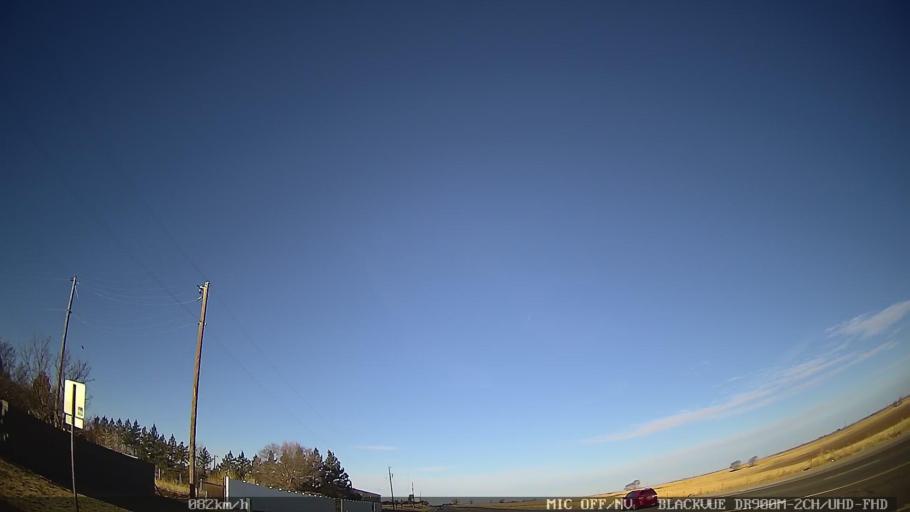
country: US
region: New Mexico
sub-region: Curry County
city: Clovis
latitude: 34.4341
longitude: -103.2343
